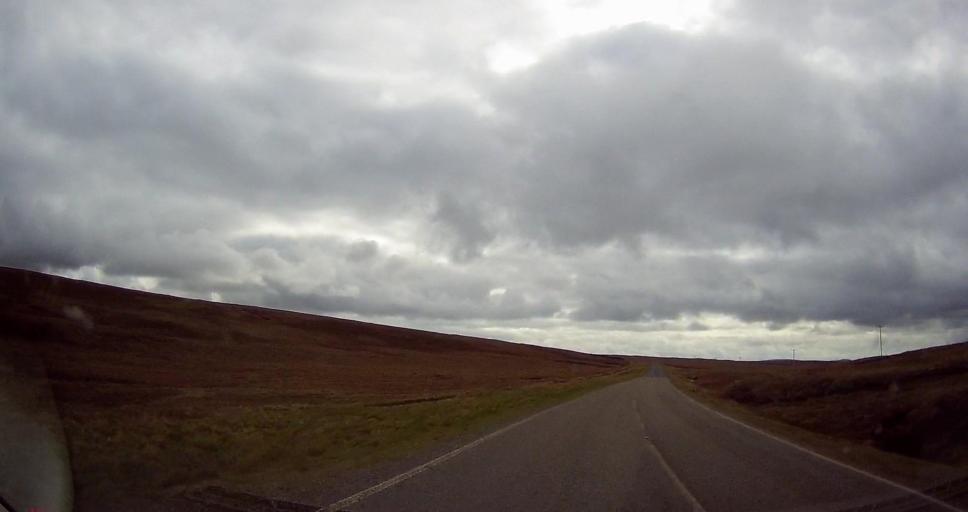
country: GB
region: Scotland
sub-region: Shetland Islands
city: Shetland
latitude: 60.6658
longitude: -1.0321
